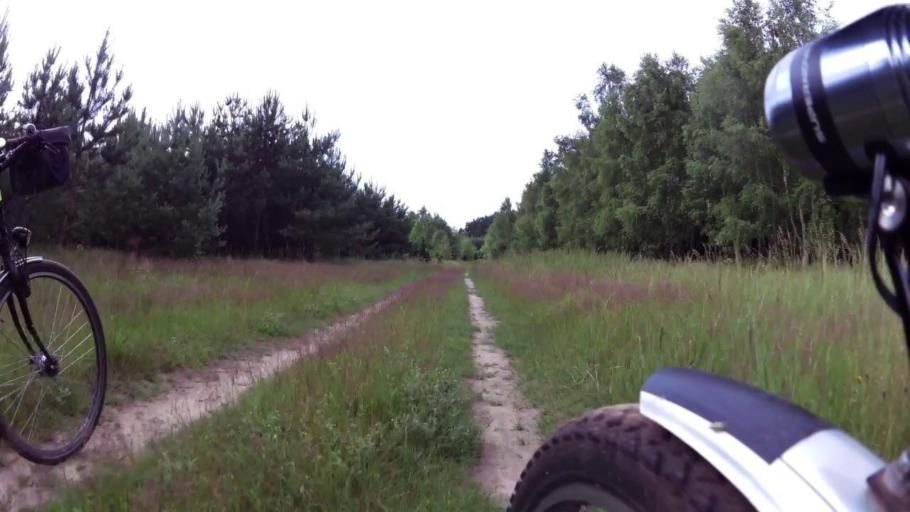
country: PL
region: West Pomeranian Voivodeship
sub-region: Powiat stargardzki
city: Dobrzany
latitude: 53.2849
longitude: 15.4113
